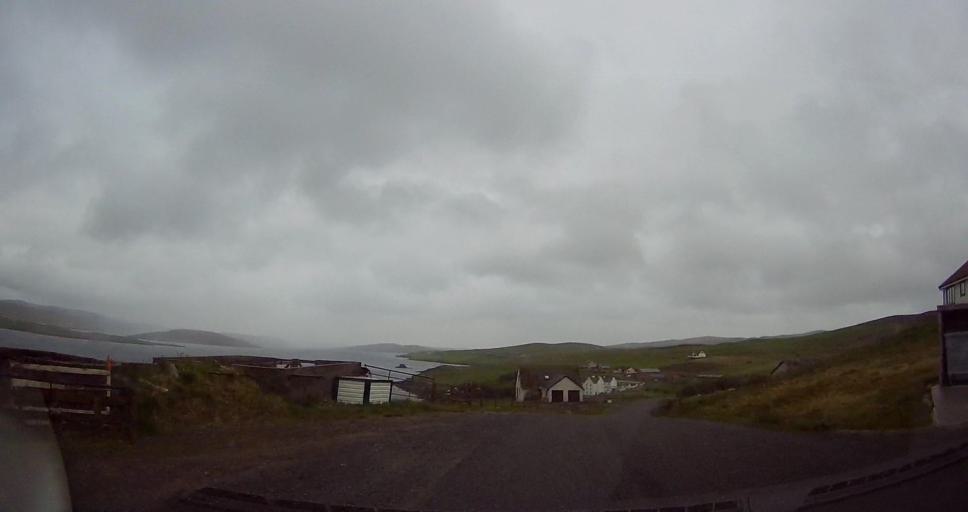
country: GB
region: Scotland
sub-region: Shetland Islands
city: Lerwick
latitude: 60.3874
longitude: -1.3722
